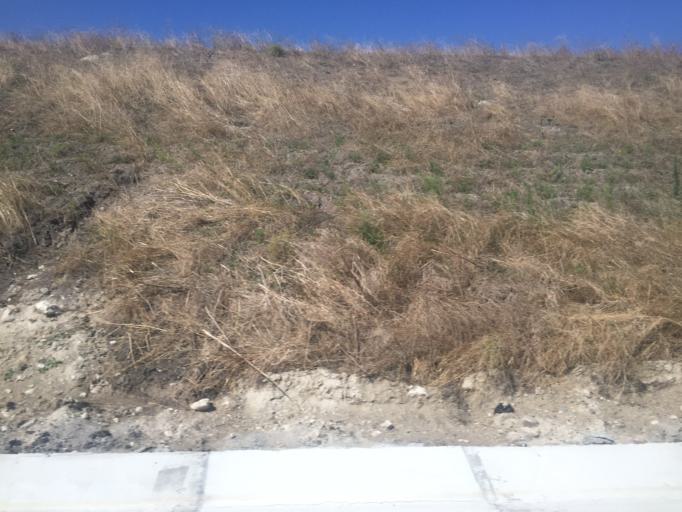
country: TR
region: Balikesir
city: Susurluk
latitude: 39.9632
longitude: 28.1644
